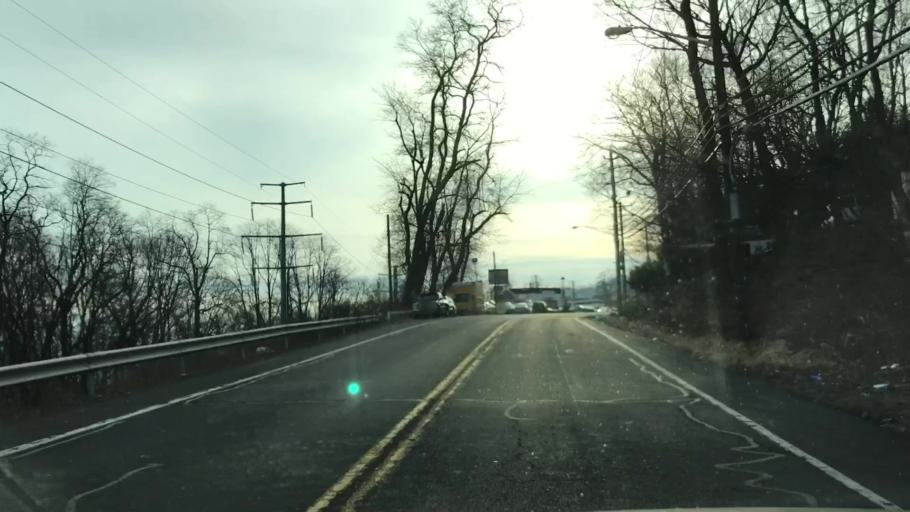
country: US
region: New York
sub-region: Rockland County
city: Haverstraw
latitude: 41.1913
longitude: -73.9641
